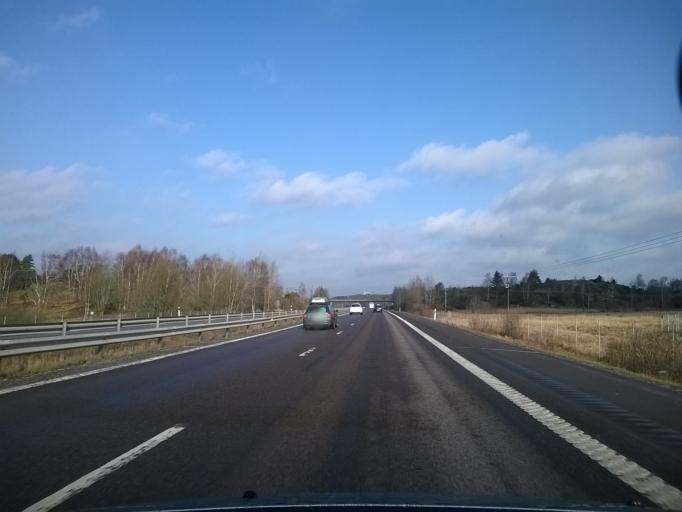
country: SE
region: Vaestra Goetaland
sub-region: Kungalvs Kommun
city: Kungalv
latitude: 57.8967
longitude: 11.9273
